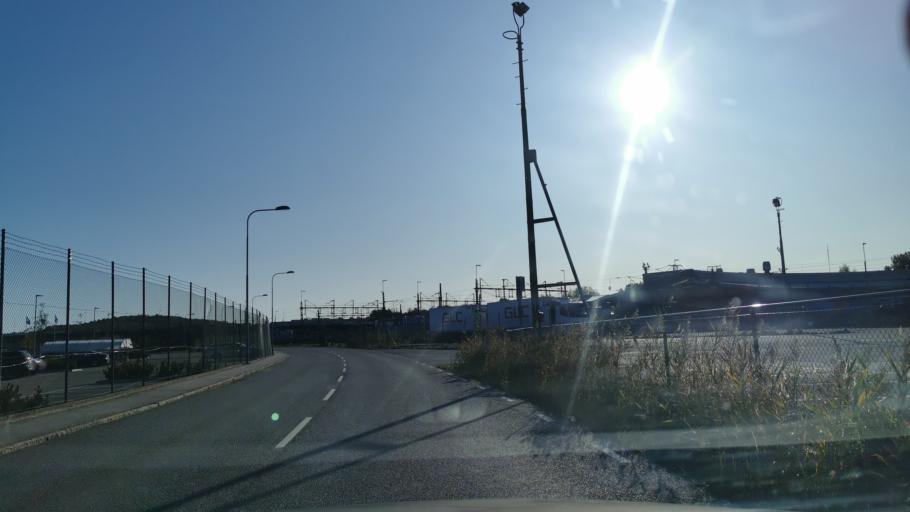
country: SE
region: Vaestra Goetaland
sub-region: Goteborg
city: Eriksbo
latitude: 57.7262
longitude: 12.0181
